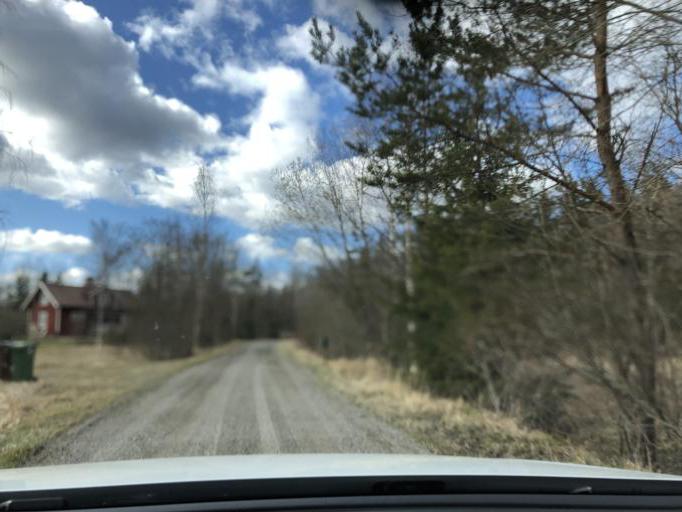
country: SE
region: Uppsala
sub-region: Tierps Kommun
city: Tierp
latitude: 60.3281
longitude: 17.3558
